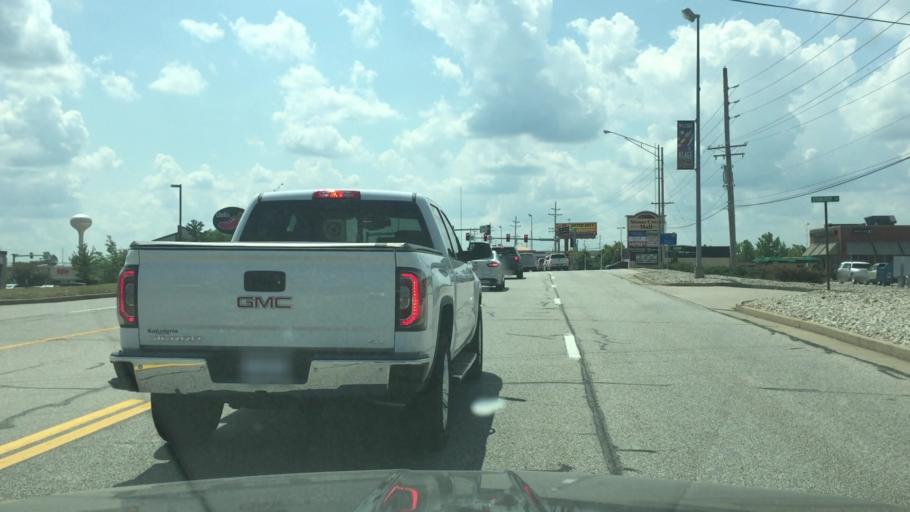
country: US
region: Missouri
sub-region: Miller County
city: Lake Ozark
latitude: 38.1628
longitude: -92.6084
